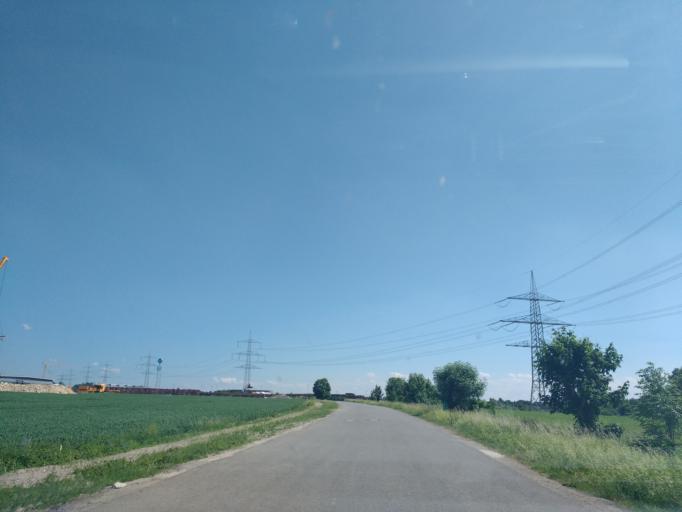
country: DE
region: North Rhine-Westphalia
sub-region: Regierungsbezirk Detmold
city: Paderborn
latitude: 51.6873
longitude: 8.7144
